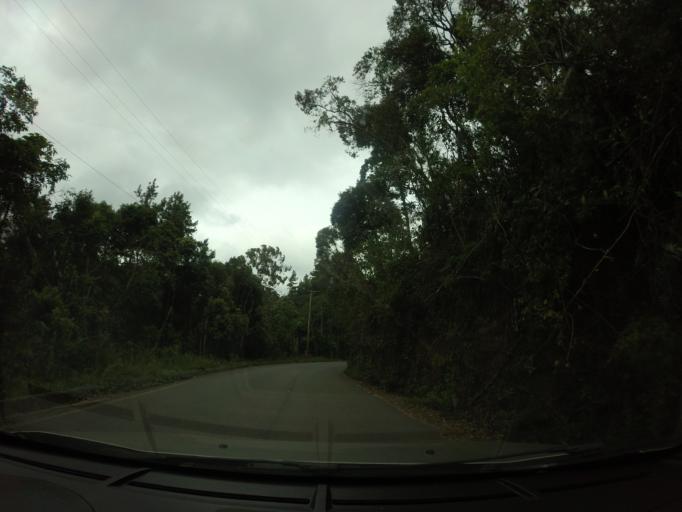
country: BR
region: Sao Paulo
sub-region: Campos Do Jordao
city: Campos do Jordao
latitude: -22.6600
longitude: -45.6018
